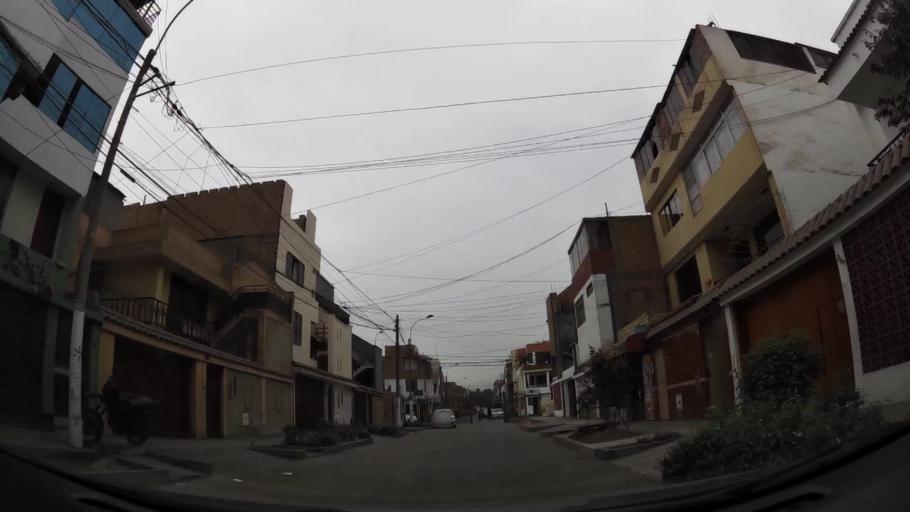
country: PE
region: Lima
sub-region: Lima
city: Independencia
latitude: -11.9677
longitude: -77.0581
